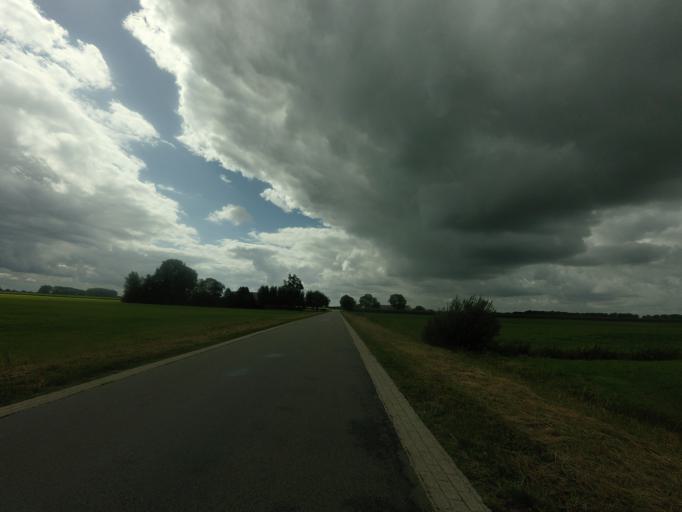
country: NL
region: Drenthe
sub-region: Gemeente Meppel
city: Meppel
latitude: 52.7153
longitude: 6.1716
